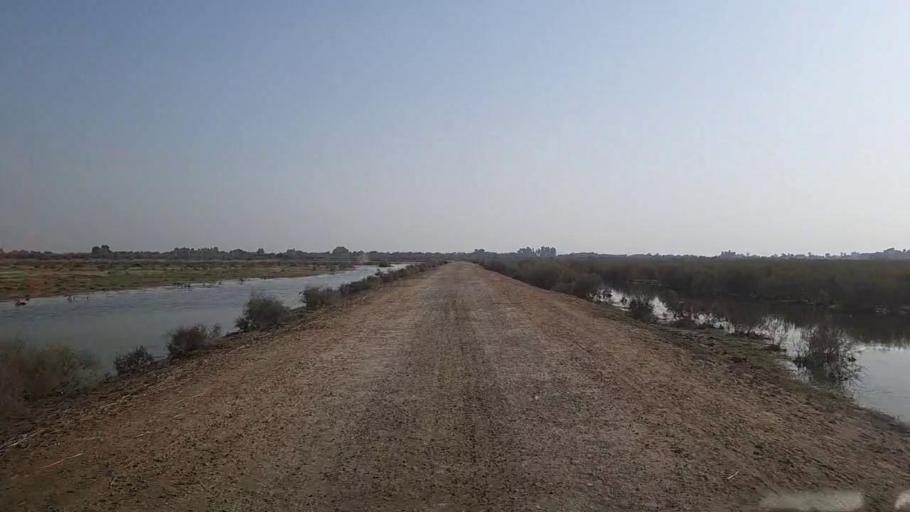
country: PK
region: Sindh
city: Kandhkot
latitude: 28.3626
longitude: 69.3301
